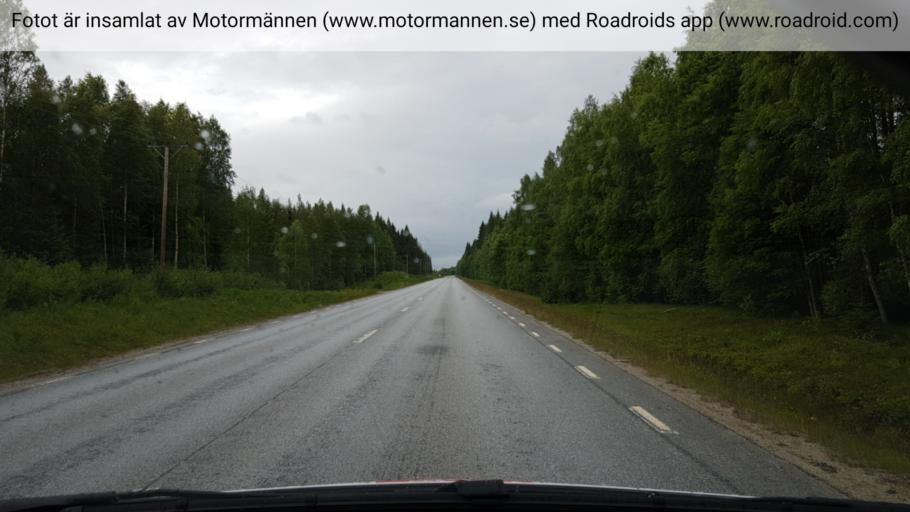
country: SE
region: Vaesterbotten
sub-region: Bjurholms Kommun
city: Bjurholm
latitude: 63.9333
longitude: 19.3458
